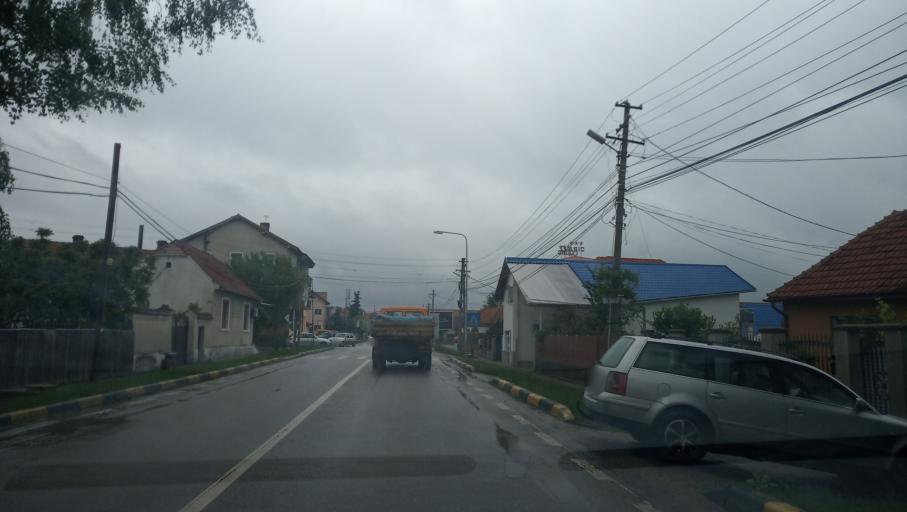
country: RO
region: Alba
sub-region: Municipiul Sebes
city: Sebes
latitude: 45.9523
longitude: 23.5811
